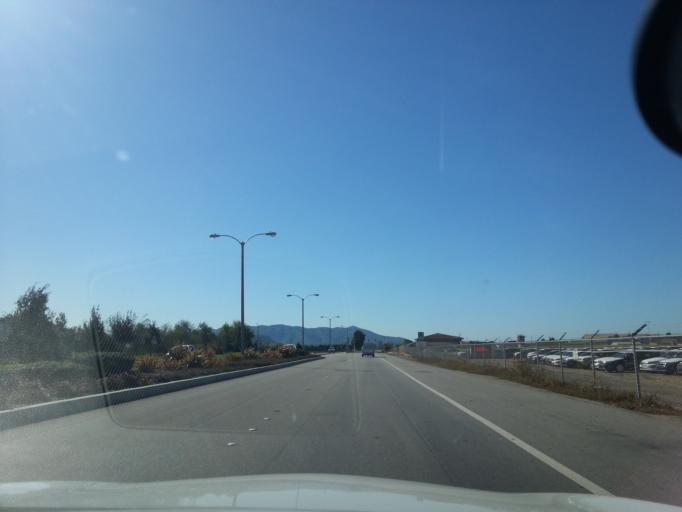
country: US
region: California
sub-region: Ventura County
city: Camarillo
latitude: 34.2150
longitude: -119.0699
